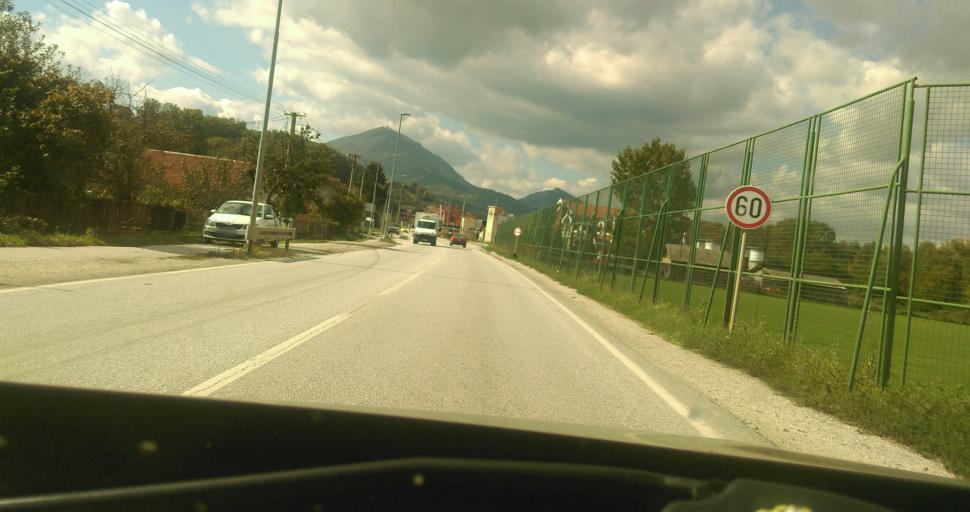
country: RS
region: Central Serbia
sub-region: Moravicki Okrug
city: Cacak
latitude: 43.8962
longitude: 20.2941
